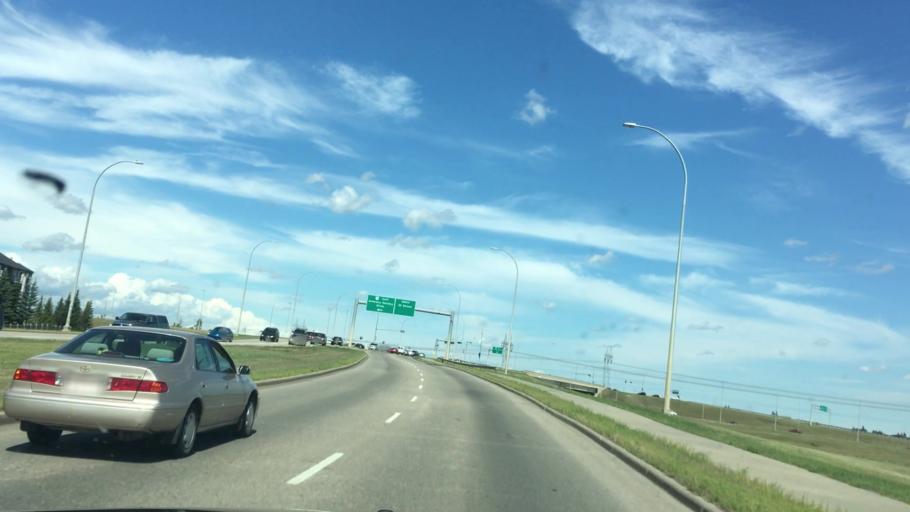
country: CA
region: Alberta
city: Beaumont
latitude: 53.4309
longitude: -113.5171
